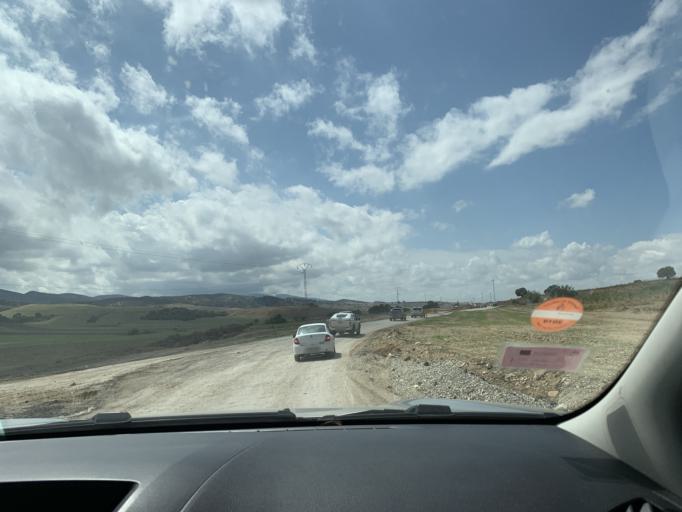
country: TN
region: Silyanah
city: Bu `Aradah
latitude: 36.1954
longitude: 9.7047
